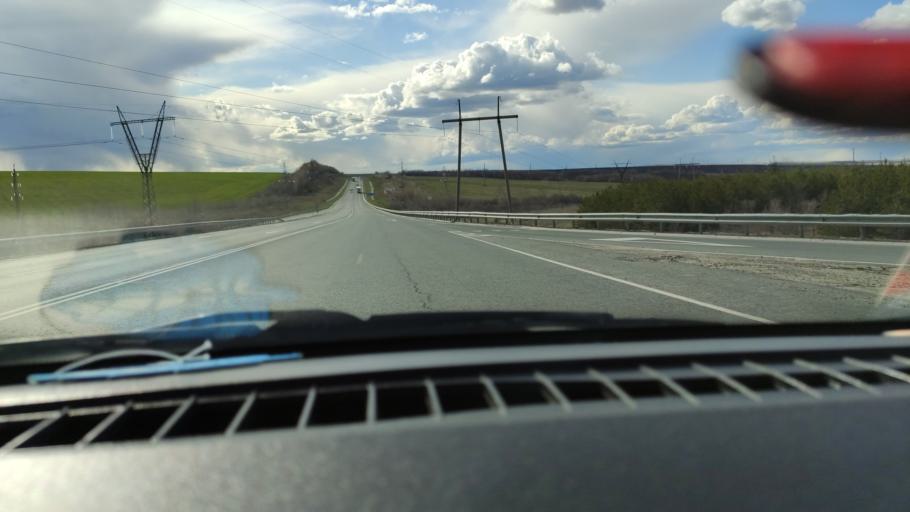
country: RU
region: Saratov
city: Shikhany
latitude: 52.1156
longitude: 47.2949
